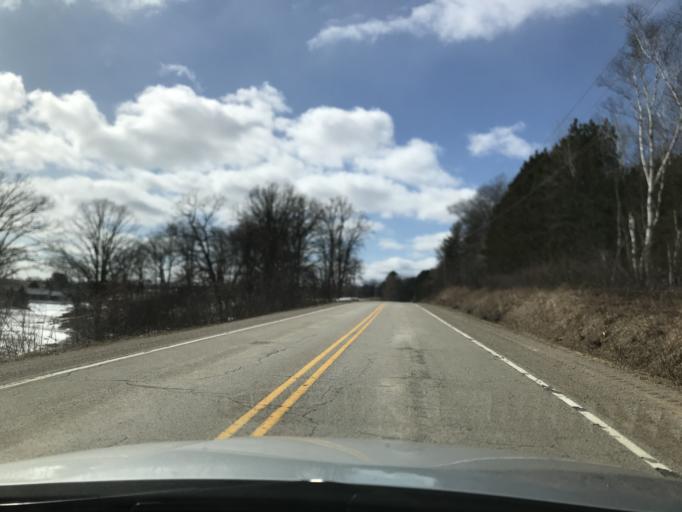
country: US
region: Wisconsin
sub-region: Oconto County
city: Oconto Falls
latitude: 45.2574
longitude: -88.0969
